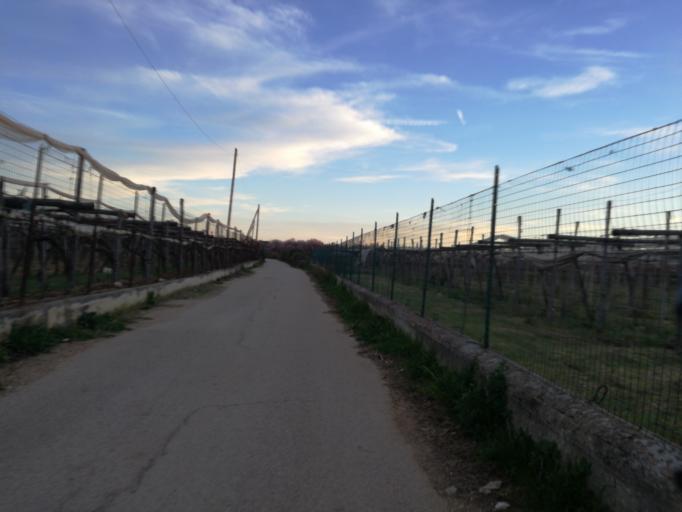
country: IT
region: Apulia
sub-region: Provincia di Bari
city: Adelfia
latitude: 41.0119
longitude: 16.8715
